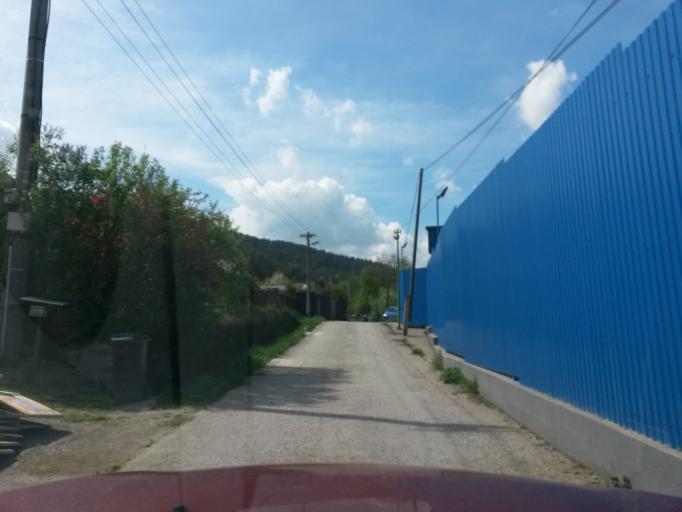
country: SK
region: Kosicky
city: Gelnica
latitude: 48.8144
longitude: 20.8931
